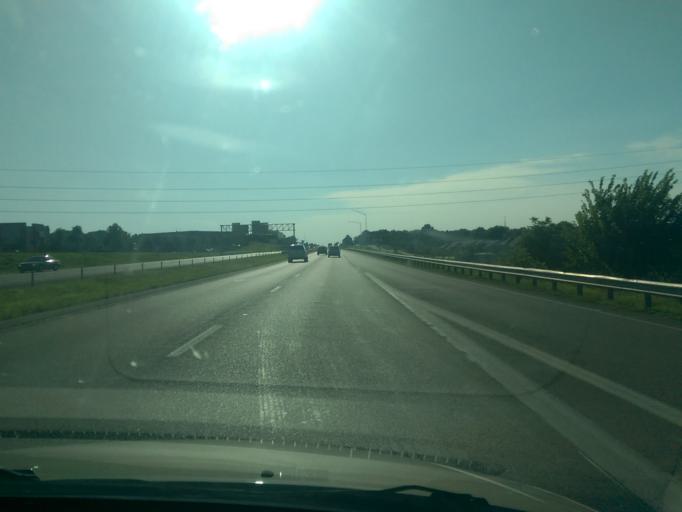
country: US
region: Missouri
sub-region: Jackson County
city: Blue Springs
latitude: 39.0281
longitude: -94.2527
